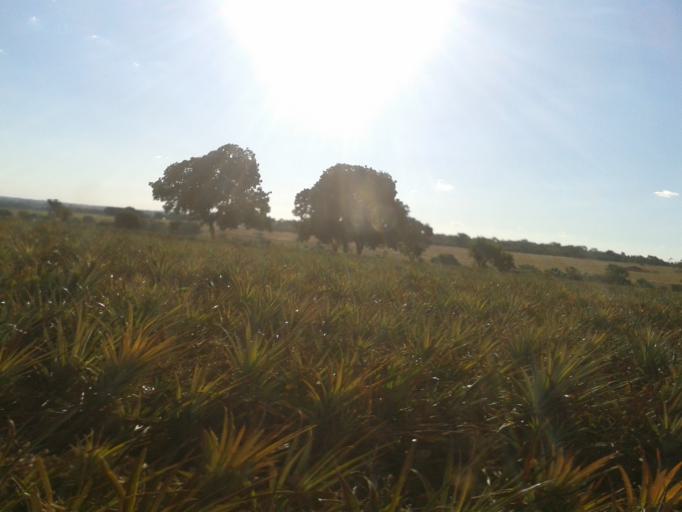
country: BR
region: Minas Gerais
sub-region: Centralina
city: Centralina
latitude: -18.7514
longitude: -49.0968
